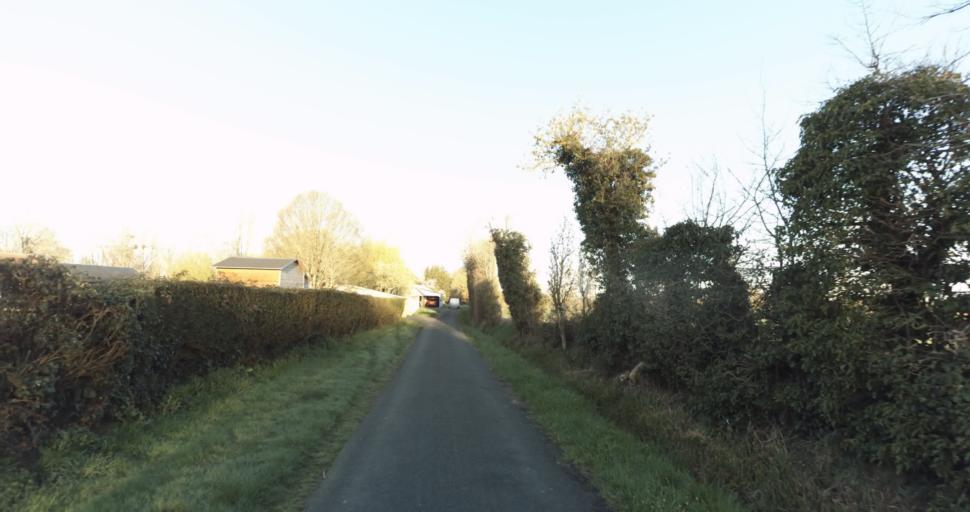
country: FR
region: Lower Normandy
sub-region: Departement du Calvados
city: Saint-Pierre-sur-Dives
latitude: 49.0240
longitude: -0.0175
